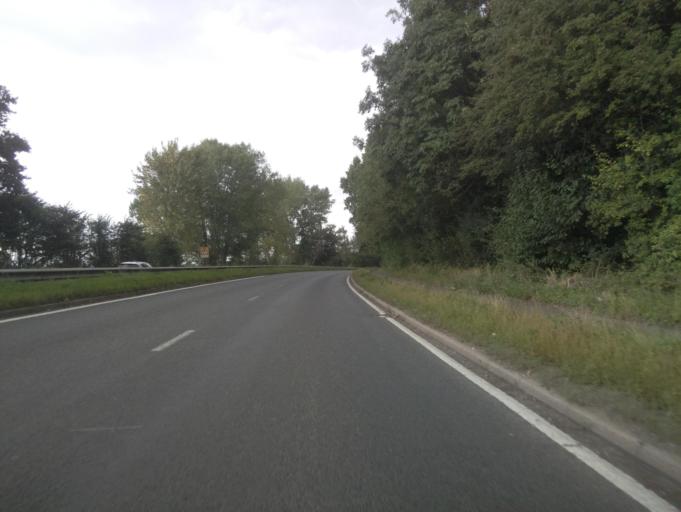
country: GB
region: England
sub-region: Warwickshire
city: Water Orton
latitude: 52.4992
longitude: -1.7132
